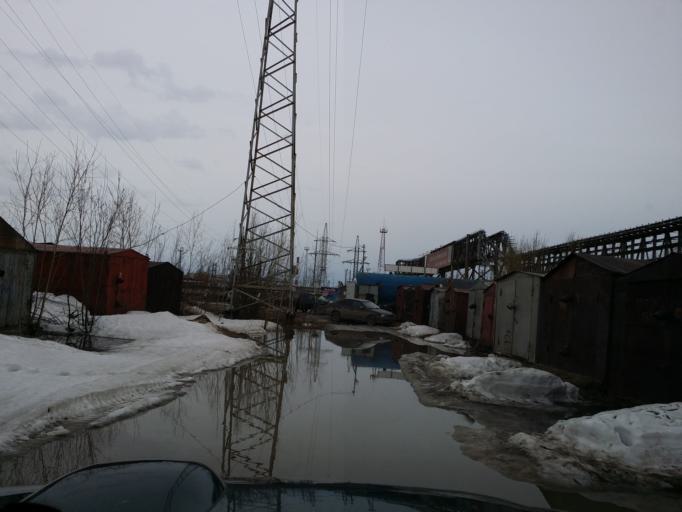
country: RU
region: Khanty-Mansiyskiy Avtonomnyy Okrug
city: Nizhnevartovsk
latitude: 60.9492
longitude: 76.5429
